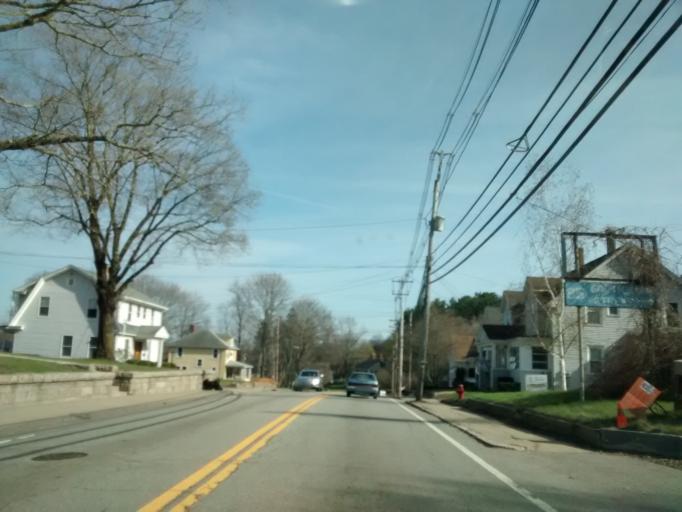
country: US
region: Massachusetts
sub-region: Worcester County
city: Uxbridge
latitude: 42.0726
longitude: -71.6267
